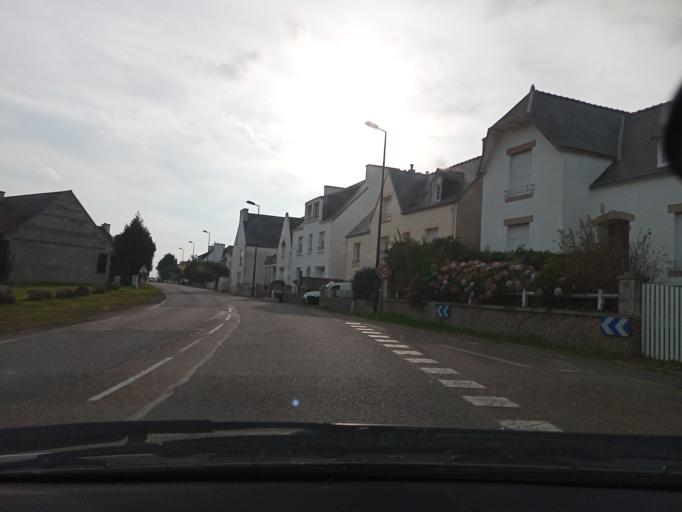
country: FR
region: Brittany
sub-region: Departement du Finistere
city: Plozevet
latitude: 47.9922
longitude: -4.4202
